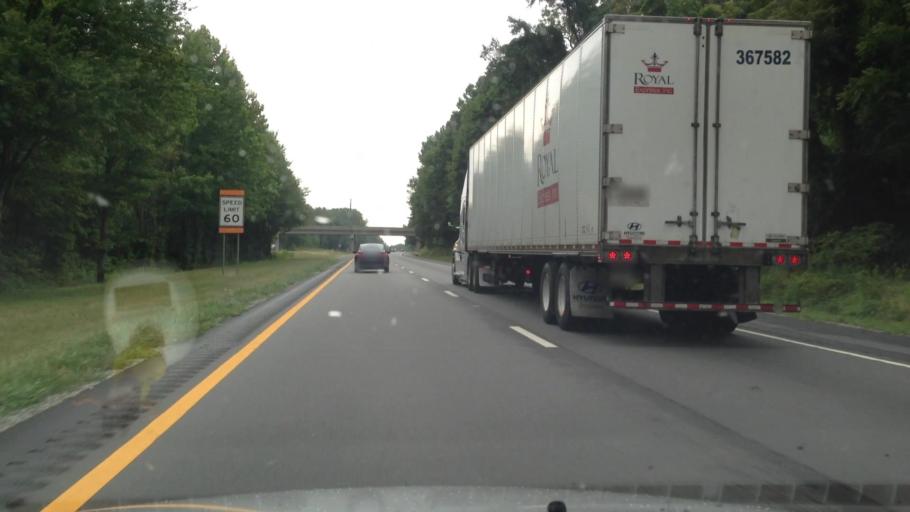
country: US
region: North Carolina
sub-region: Forsyth County
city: Kernersville
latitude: 36.0981
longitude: -80.0152
